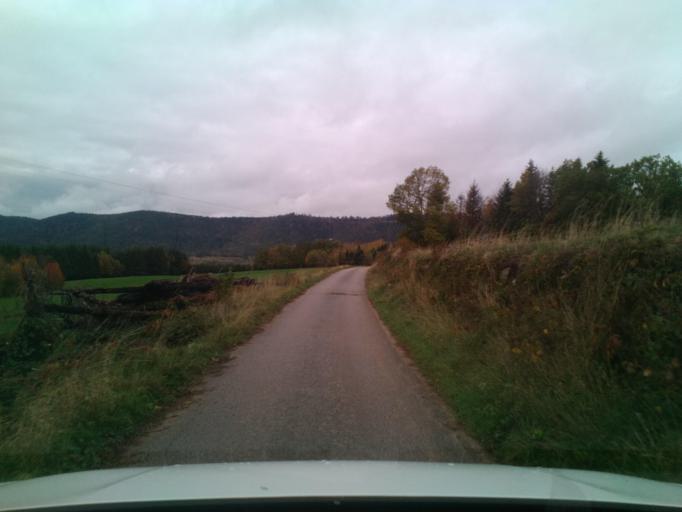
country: FR
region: Lorraine
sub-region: Departement des Vosges
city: Senones
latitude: 48.3822
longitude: 6.9881
